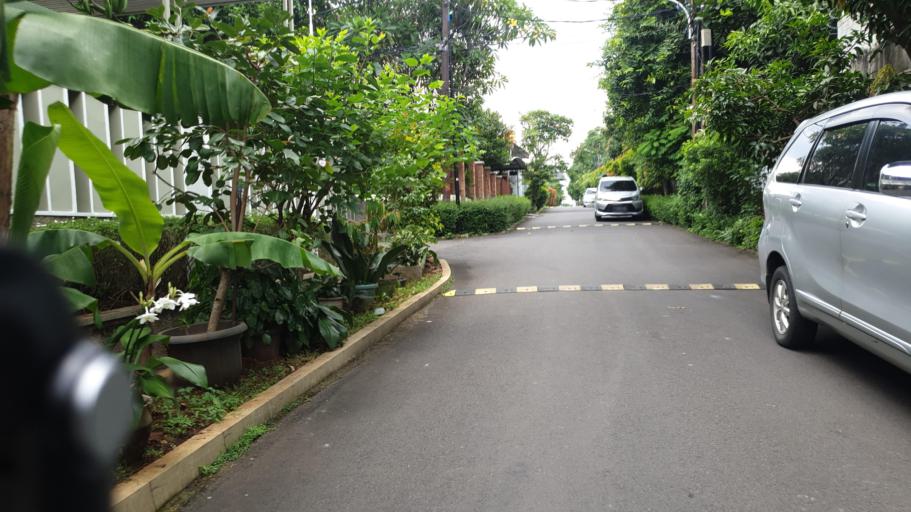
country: ID
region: Banten
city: South Tangerang
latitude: -6.2887
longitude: 106.7939
